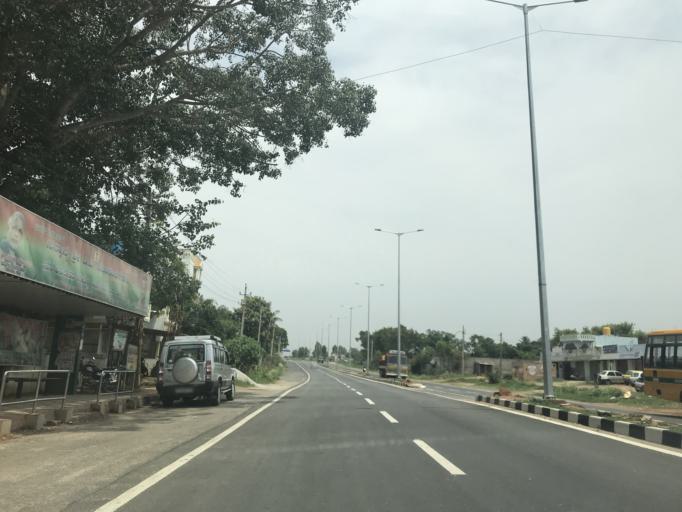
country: IN
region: Karnataka
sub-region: Bangalore Urban
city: Yelahanka
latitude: 13.1224
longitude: 77.6683
